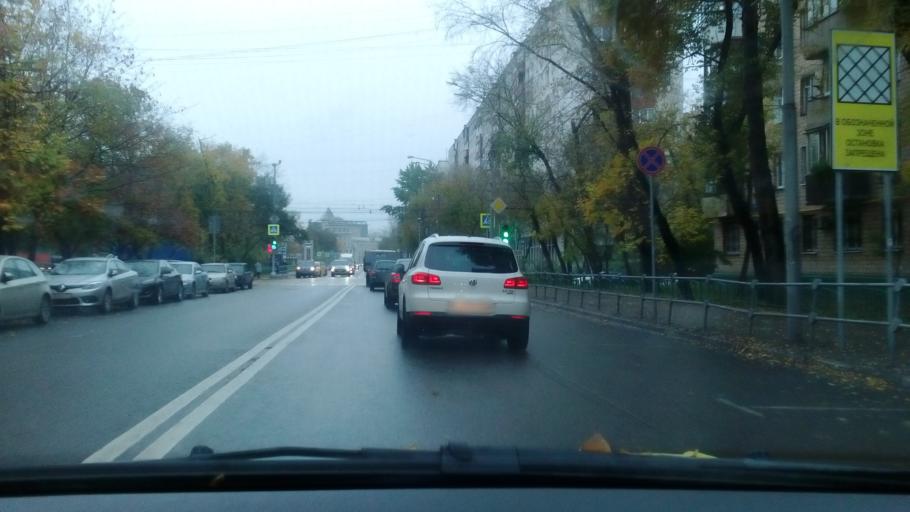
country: RU
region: Moscow
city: Mar'ina Roshcha
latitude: 55.7956
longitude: 37.5765
